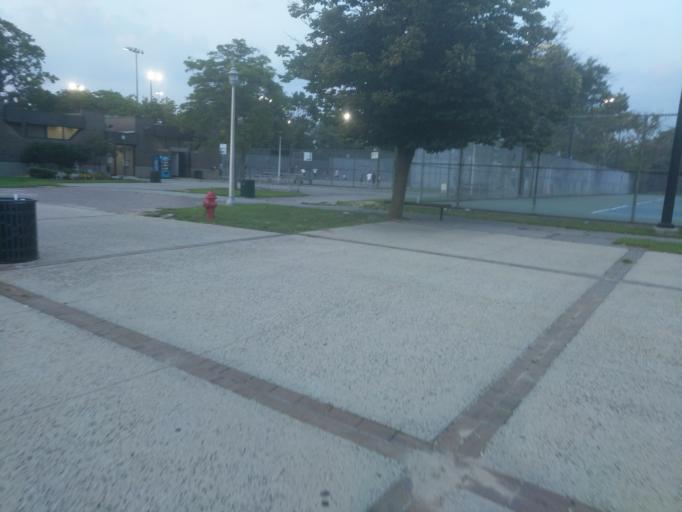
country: US
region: New York
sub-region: Nassau County
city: South Valley Stream
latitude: 40.6455
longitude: -73.7368
